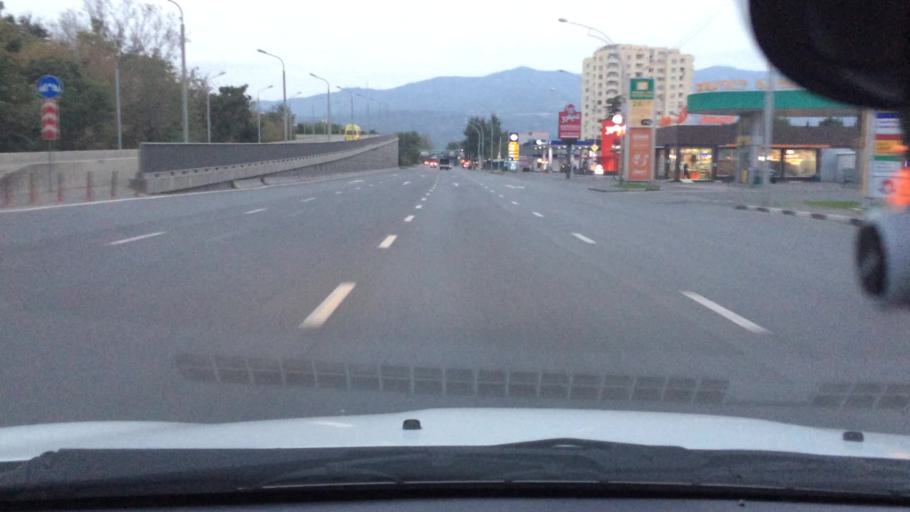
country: GE
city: Zahesi
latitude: 41.7934
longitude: 44.7706
